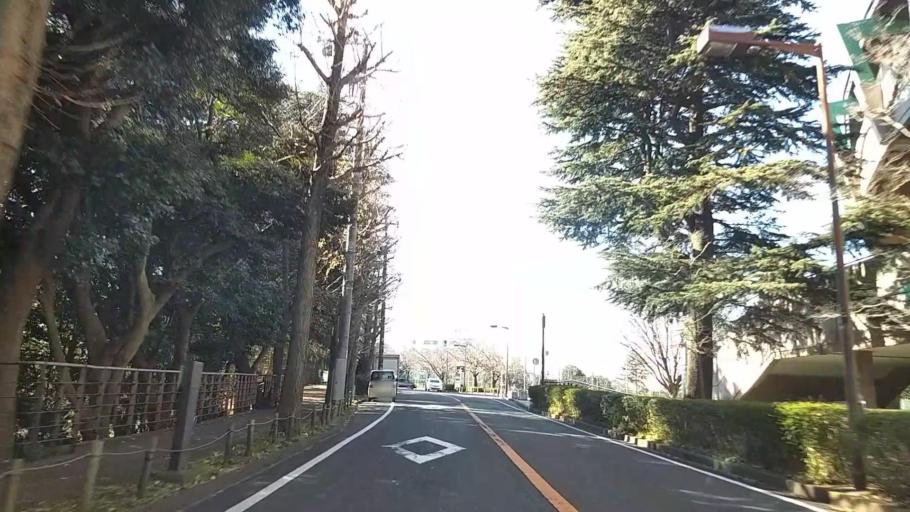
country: JP
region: Kanagawa
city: Yokohama
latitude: 35.4533
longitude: 139.5828
